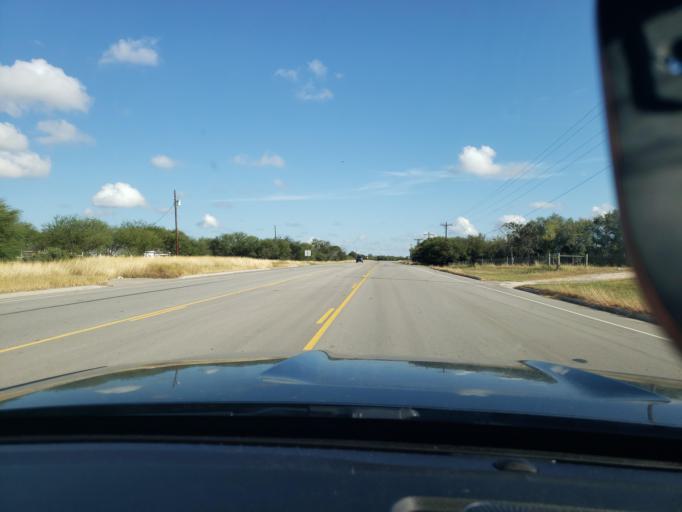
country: US
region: Texas
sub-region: Bee County
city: Beeville
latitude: 28.4358
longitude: -97.7132
